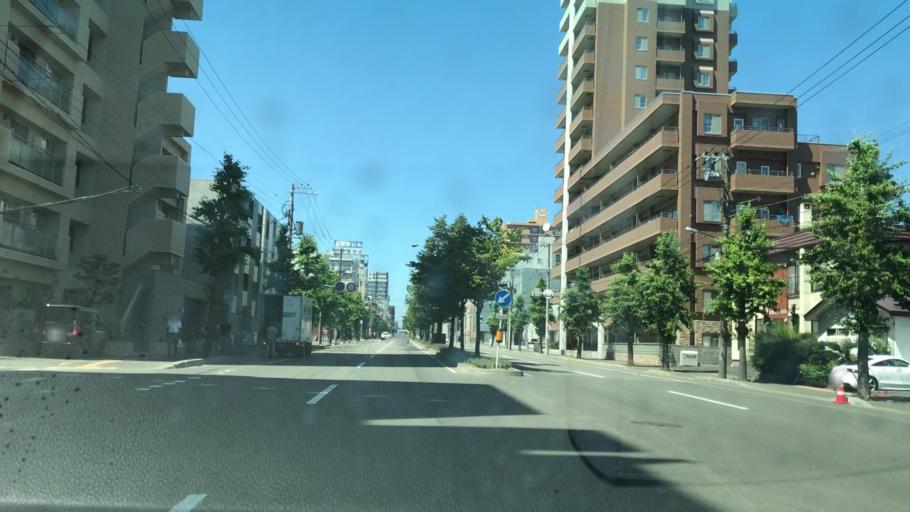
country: JP
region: Hokkaido
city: Sapporo
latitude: 43.0719
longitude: 141.3105
